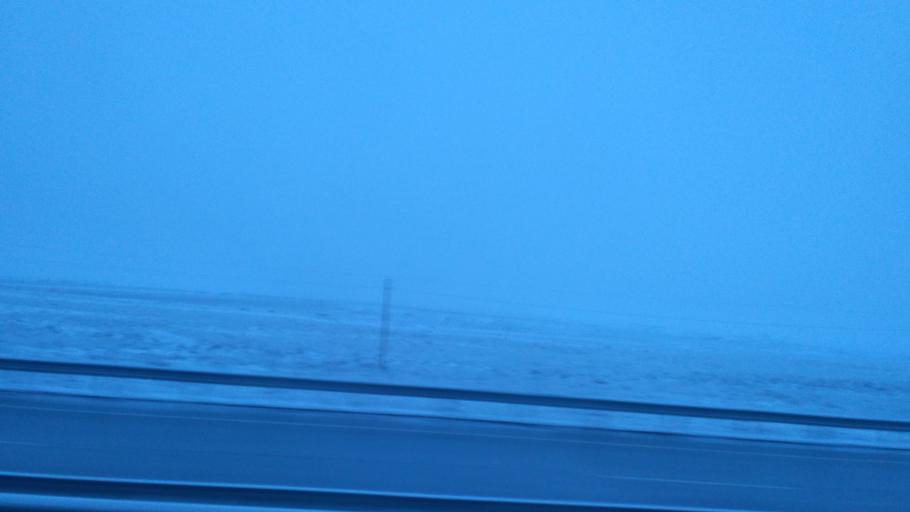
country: KZ
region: Ongtustik Qazaqstan
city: Shymkent
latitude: 42.4274
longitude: 69.4363
